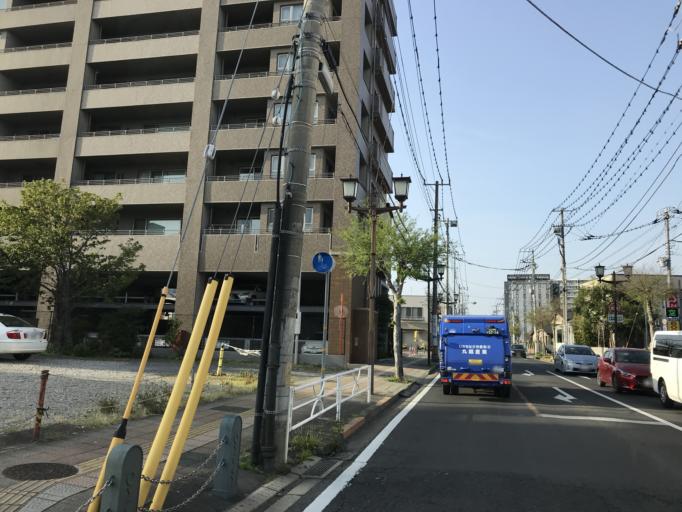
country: JP
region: Ibaraki
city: Hitachi-Naka
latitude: 36.3949
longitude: 140.5263
